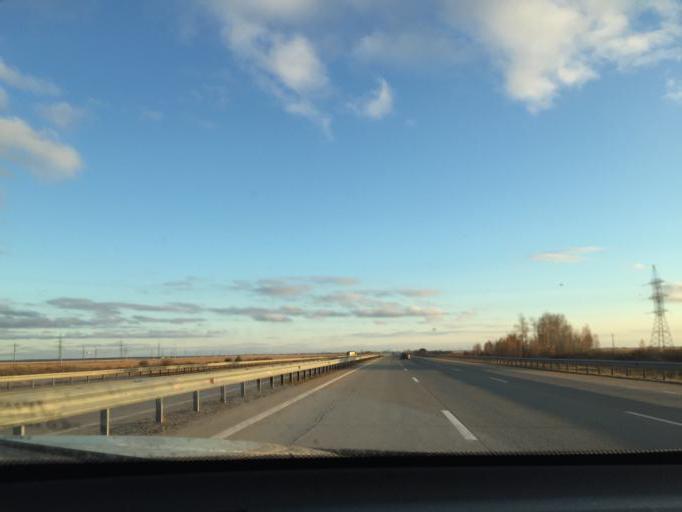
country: KZ
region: Astana Qalasy
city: Astana
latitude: 51.2980
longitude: 71.3566
